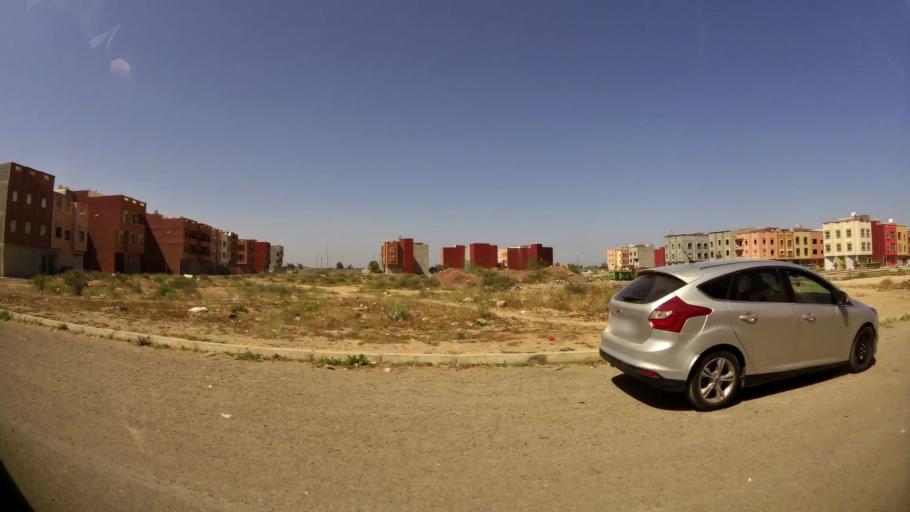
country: MA
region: Souss-Massa-Draa
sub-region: Inezgane-Ait Mellou
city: Inezgane
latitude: 30.3325
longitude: -9.5094
